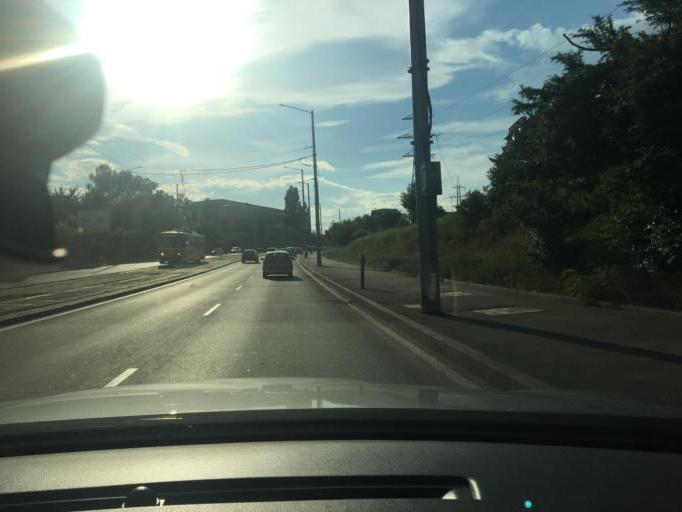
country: BG
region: Sofia-Capital
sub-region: Stolichna Obshtina
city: Sofia
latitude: 42.6756
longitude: 23.3737
